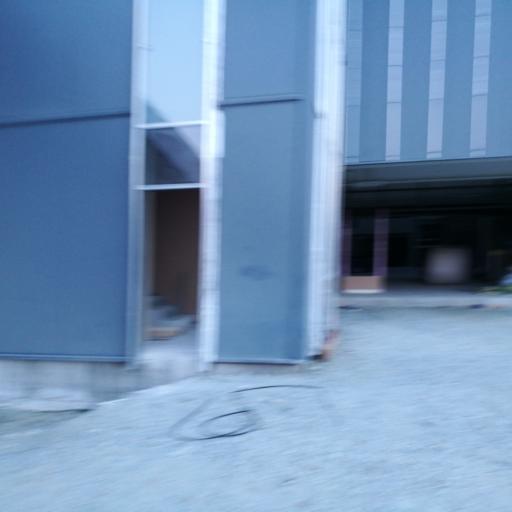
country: RO
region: Constanta
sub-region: Municipiul Constanta
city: Palazu Mare
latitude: 44.2008
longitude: 28.6065
